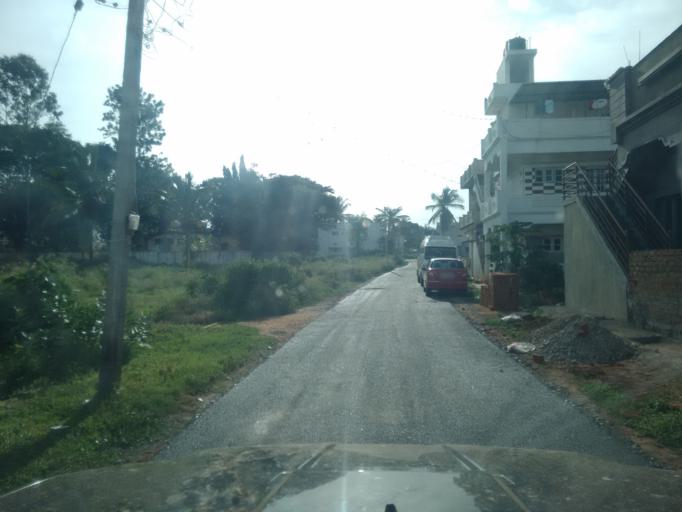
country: IN
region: Karnataka
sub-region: Tumkur
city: Gubbi
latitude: 13.3199
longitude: 76.9403
